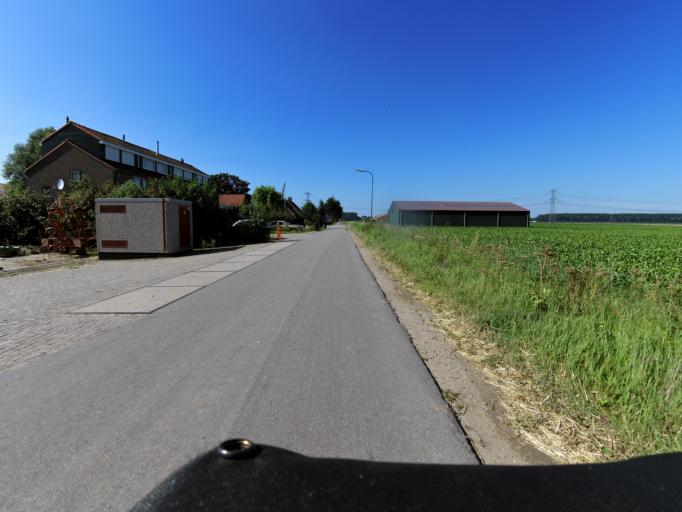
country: NL
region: South Holland
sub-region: Gemeente Dordrecht
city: Dordrecht
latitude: 51.7677
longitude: 4.7132
